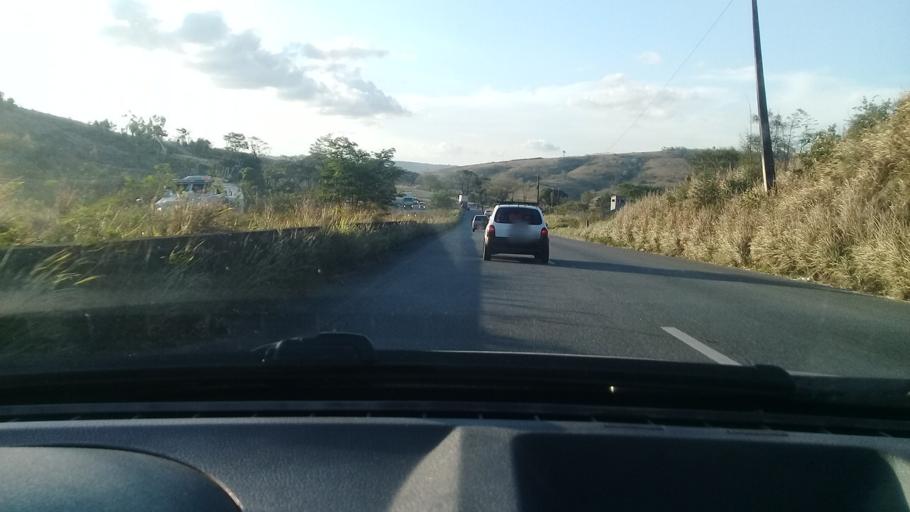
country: BR
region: Pernambuco
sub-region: Vitoria De Santo Antao
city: Vitoria de Santo Antao
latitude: -8.1171
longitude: -35.2346
